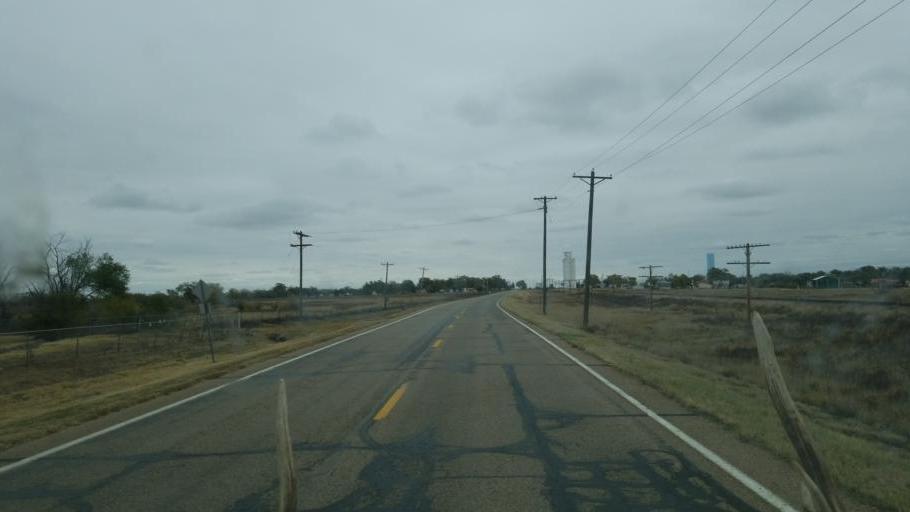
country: US
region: Colorado
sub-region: Crowley County
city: Ordway
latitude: 38.2326
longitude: -103.6725
